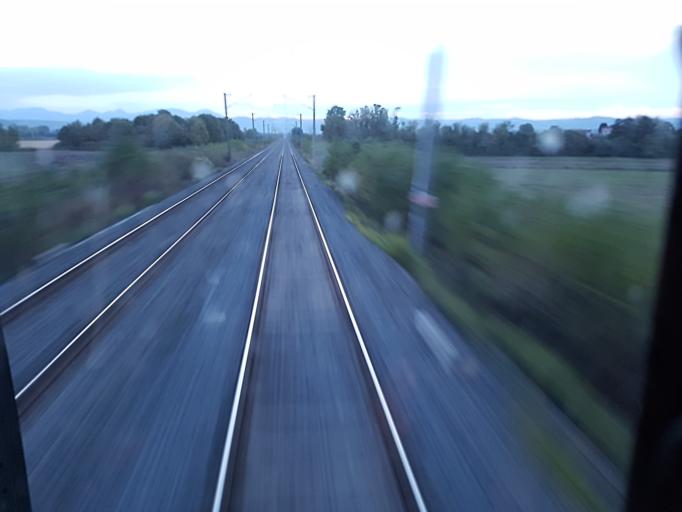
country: FR
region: Auvergne
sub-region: Departement du Puy-de-Dome
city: Ennezat
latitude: 45.9065
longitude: 3.1836
